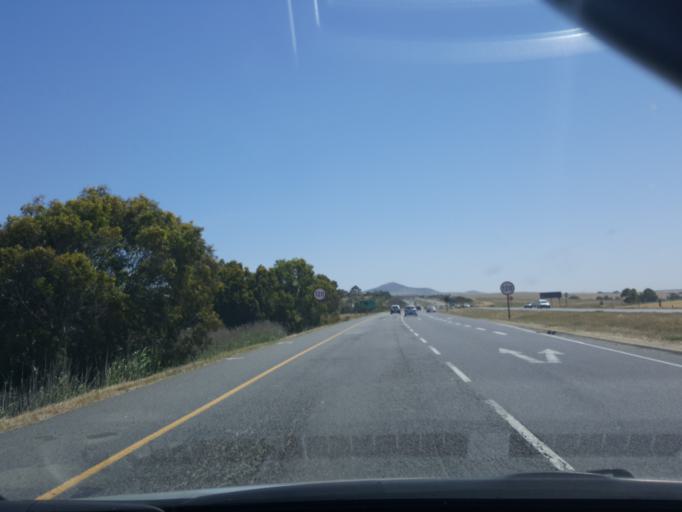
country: ZA
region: Western Cape
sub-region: City of Cape Town
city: Sunset Beach
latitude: -33.7936
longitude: 18.5478
